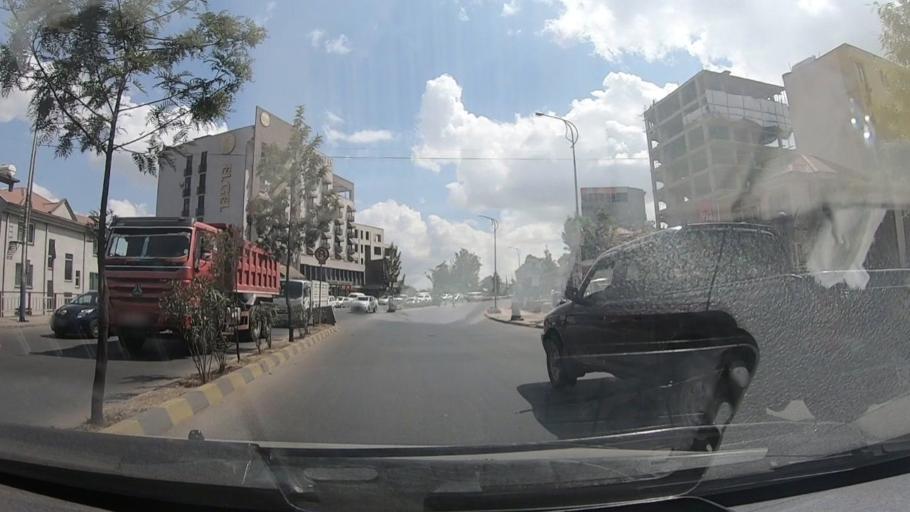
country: ET
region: Adis Abeba
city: Addis Ababa
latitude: 8.9804
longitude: 38.7215
